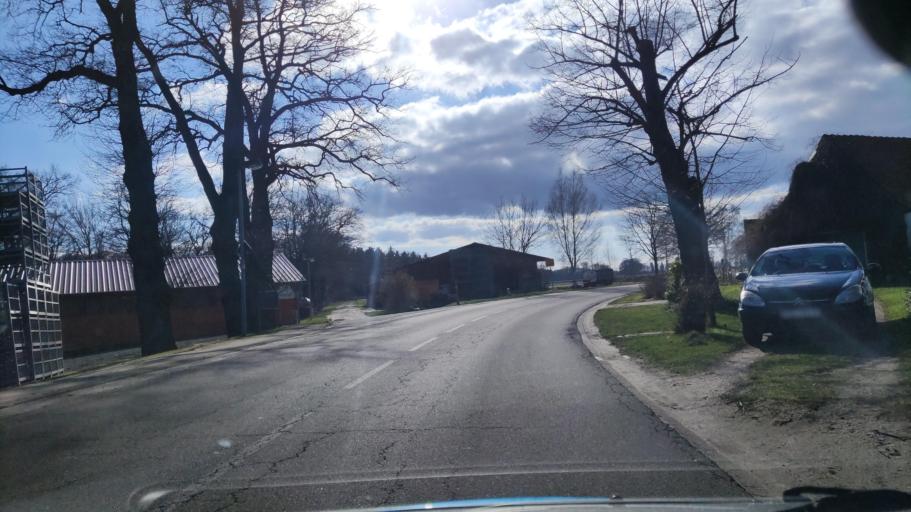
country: DE
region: Lower Saxony
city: Eldingen
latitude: 52.6700
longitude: 10.3035
